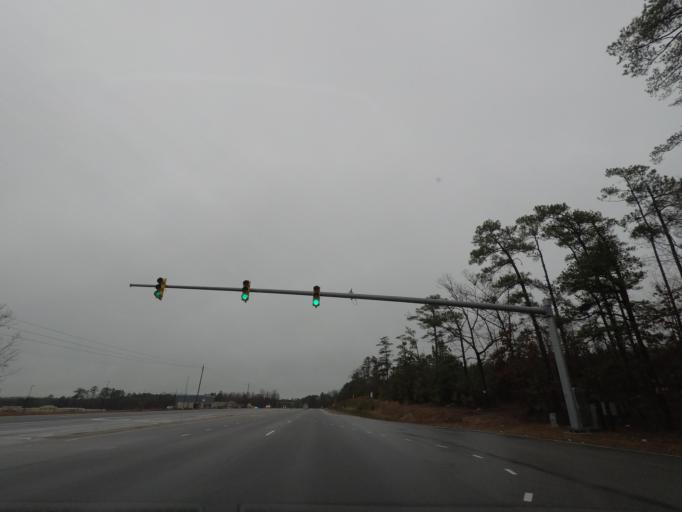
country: US
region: North Carolina
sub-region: Cumberland County
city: Spring Lake
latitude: 35.2431
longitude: -79.0220
